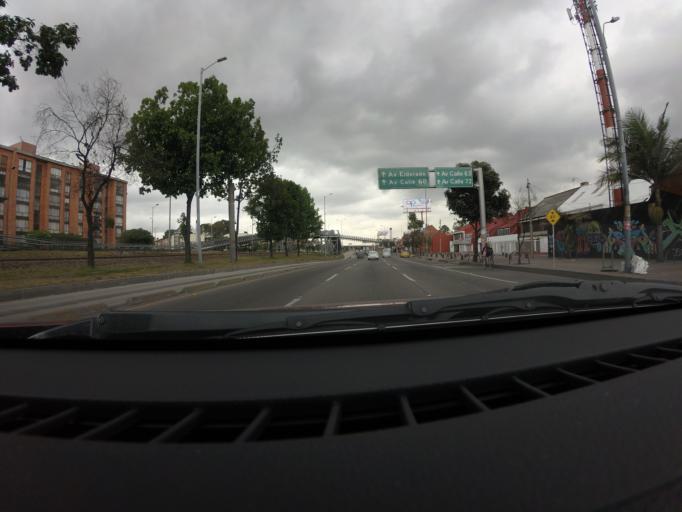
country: CO
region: Bogota D.C.
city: Barrio San Luis
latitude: 4.6755
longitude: -74.0650
